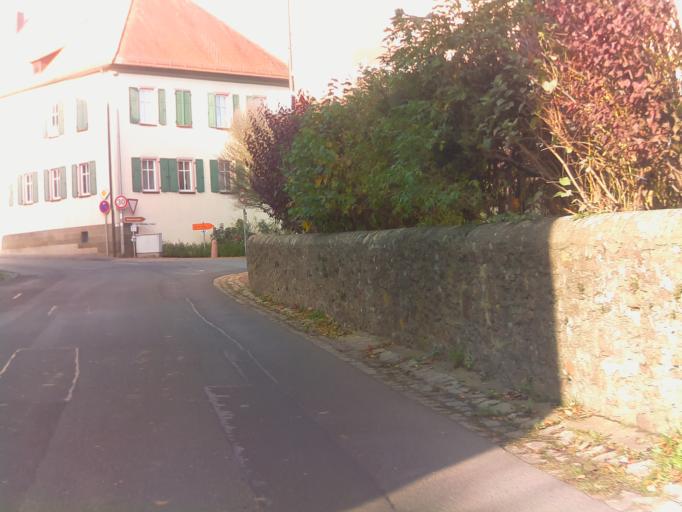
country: DE
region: Bavaria
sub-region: Regierungsbezirk Unterfranken
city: Bad Bocklet
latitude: 50.2558
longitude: 10.0610
